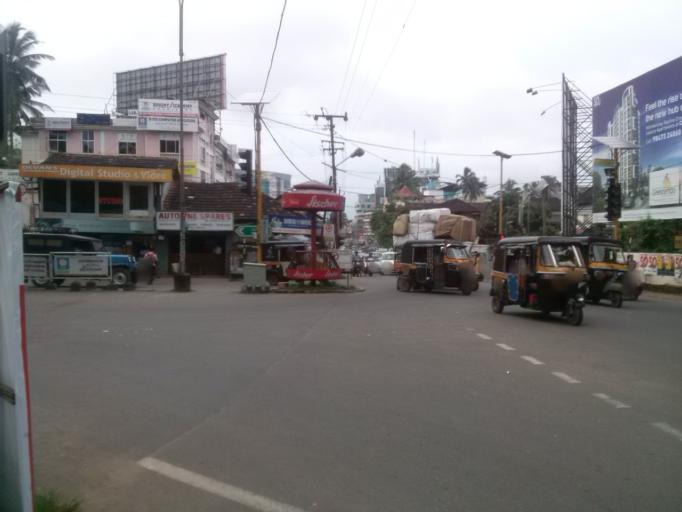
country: IN
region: Kerala
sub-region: Kozhikode
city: Kozhikode
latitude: 11.2566
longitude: 75.7805
